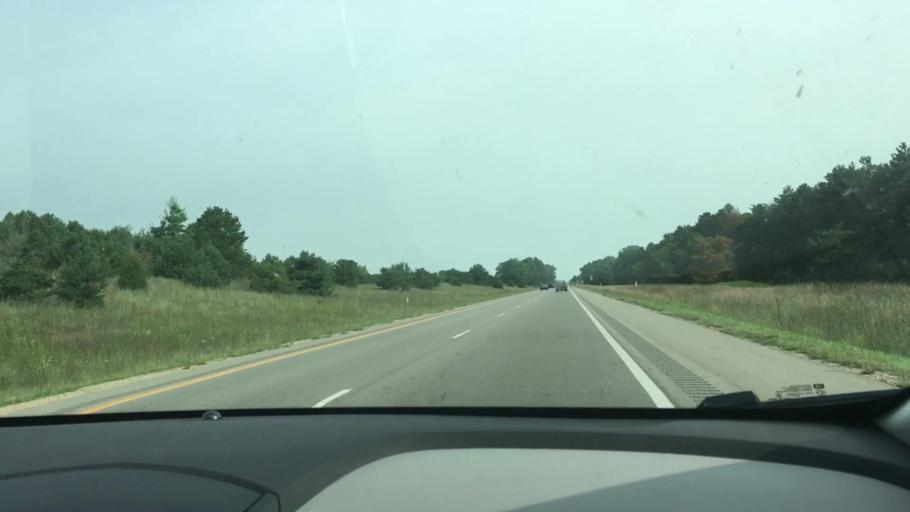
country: US
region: Michigan
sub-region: Kalamazoo County
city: Schoolcraft
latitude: 42.1604
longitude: -85.6440
